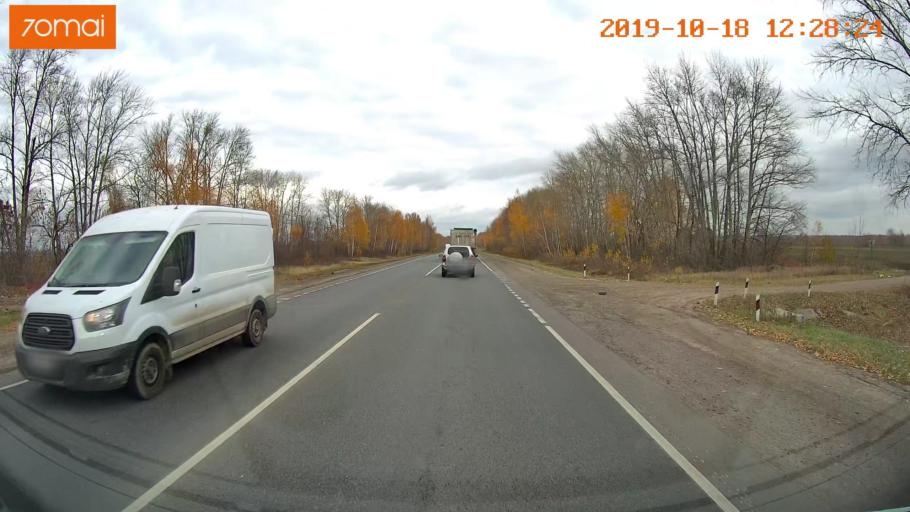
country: RU
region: Rjazan
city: Ryazan'
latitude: 54.5718
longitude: 39.5680
